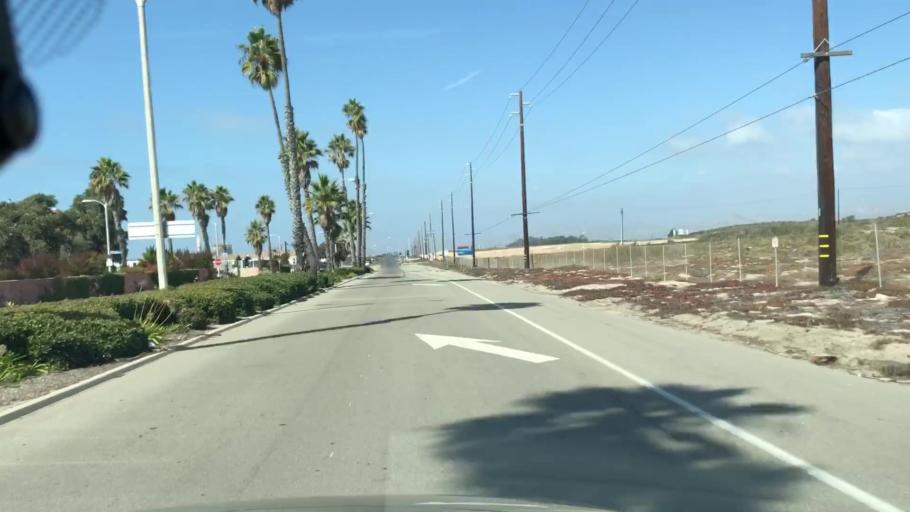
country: US
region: California
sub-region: Ventura County
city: Oxnard Shores
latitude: 34.1953
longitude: -119.2410
